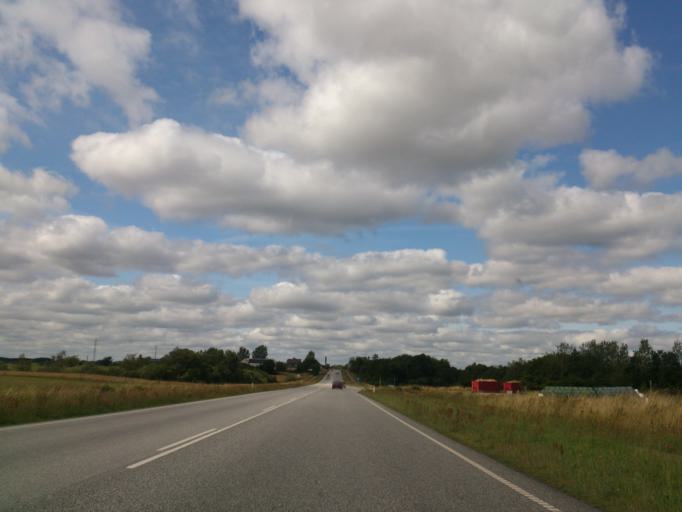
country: DK
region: South Denmark
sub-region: Aabenraa Kommune
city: Aabenraa
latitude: 54.9736
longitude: 9.4476
